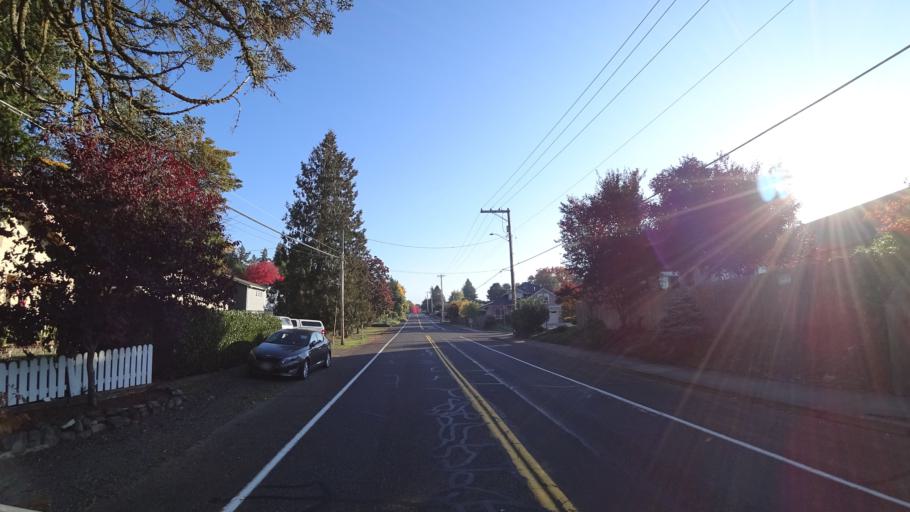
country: US
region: Oregon
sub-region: Multnomah County
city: Gresham
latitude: 45.4843
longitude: -122.4532
